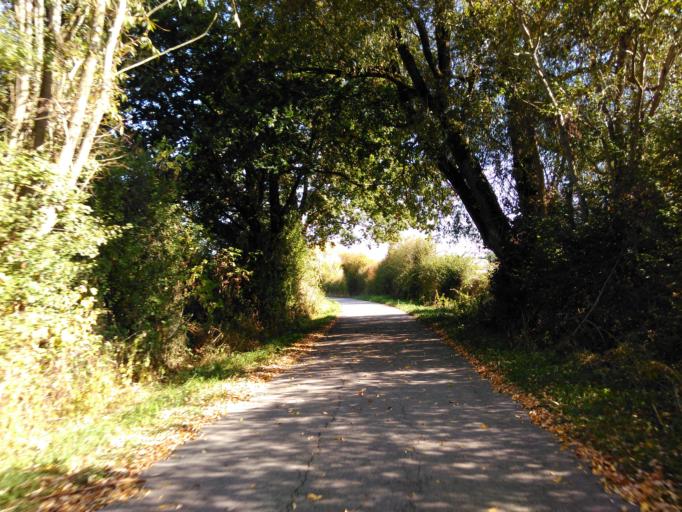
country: LU
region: Diekirch
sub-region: Canton de Redange
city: Beckerich
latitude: 49.7382
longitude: 5.9211
